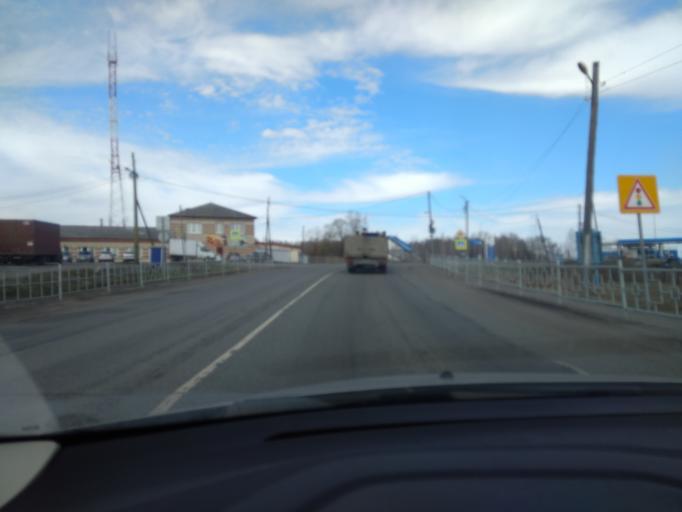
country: RU
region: Sverdlovsk
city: Pyshma
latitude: 56.9510
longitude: 63.2265
